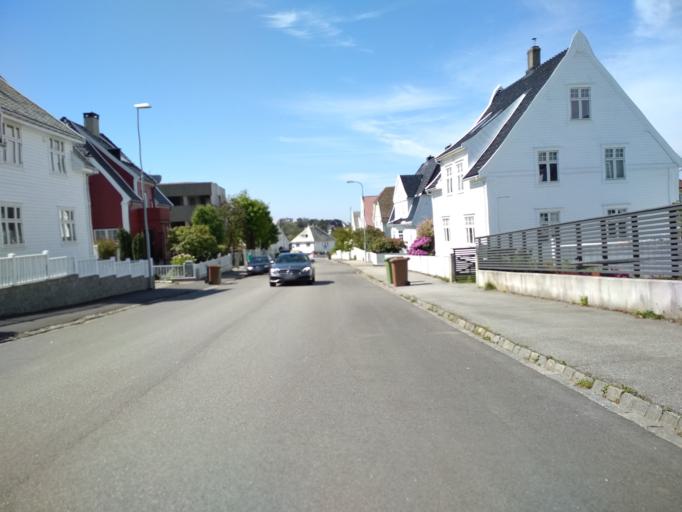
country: NO
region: Rogaland
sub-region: Stavanger
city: Stavanger
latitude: 58.9594
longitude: 5.7275
